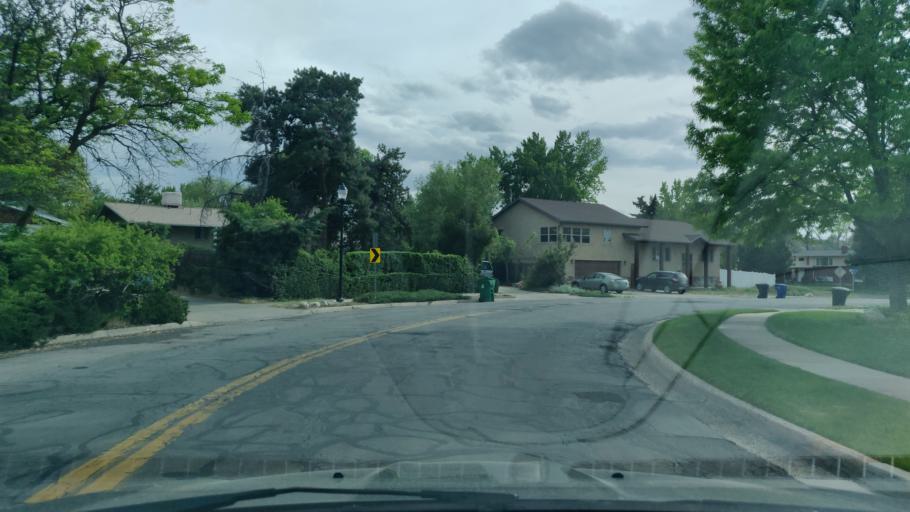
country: US
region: Utah
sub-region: Salt Lake County
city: Little Cottonwood Creek Valley
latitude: 40.6303
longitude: -111.8434
